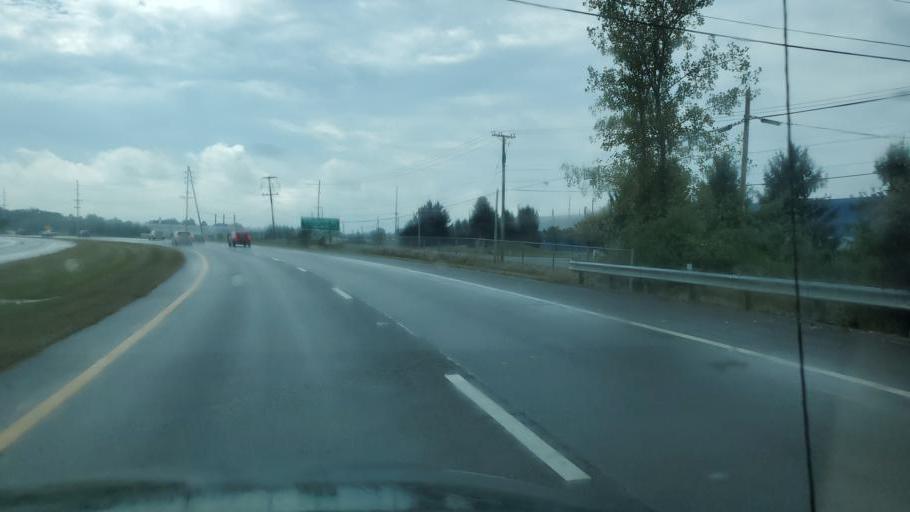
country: US
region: Ohio
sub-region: Licking County
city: Hebron
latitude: 39.9735
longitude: -82.4883
